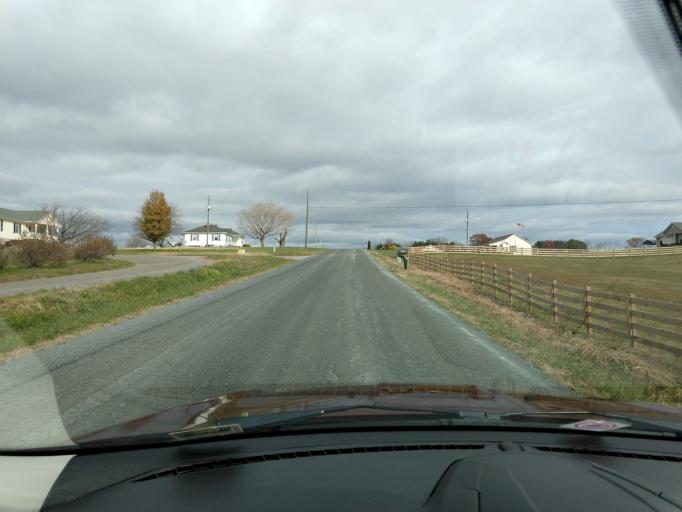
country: US
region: Virginia
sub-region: Franklin County
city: North Shore
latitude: 37.2098
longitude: -79.6811
